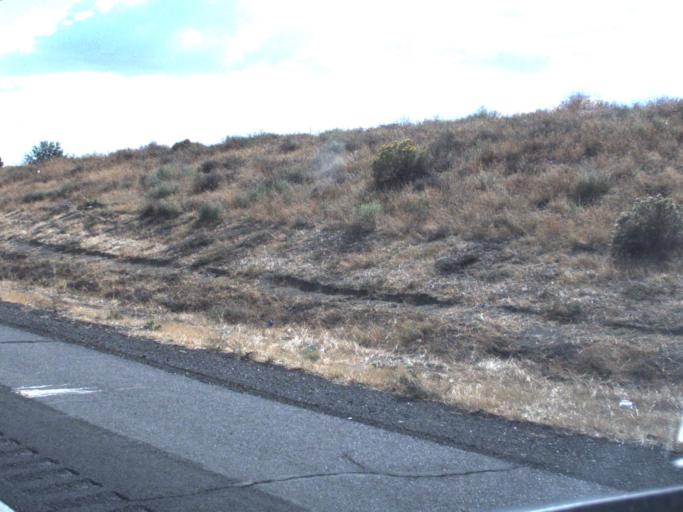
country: US
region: Washington
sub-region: Yakima County
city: Zillah
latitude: 46.3795
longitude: -120.2230
